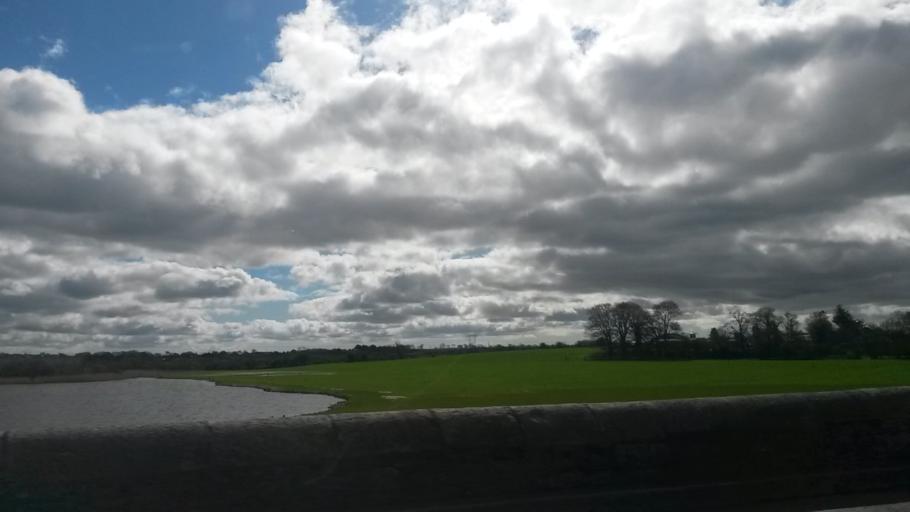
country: IE
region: Munster
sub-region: County Cork
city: Carrigtwohill
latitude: 51.9021
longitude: -8.2813
